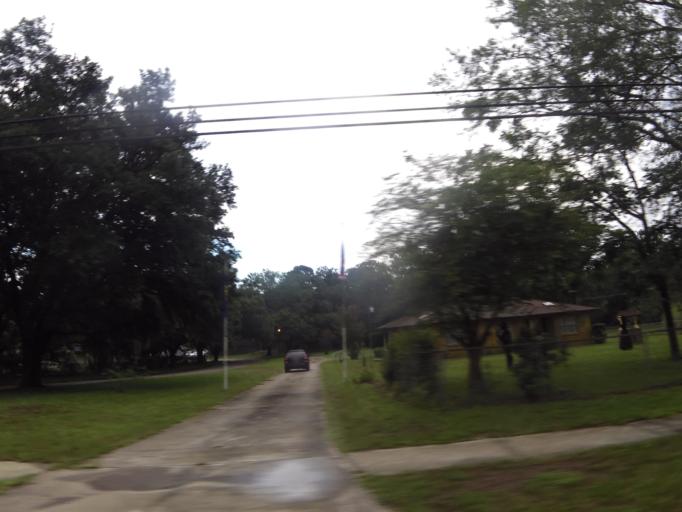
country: US
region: Florida
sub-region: Duval County
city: Jacksonville
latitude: 30.3162
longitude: -81.5418
